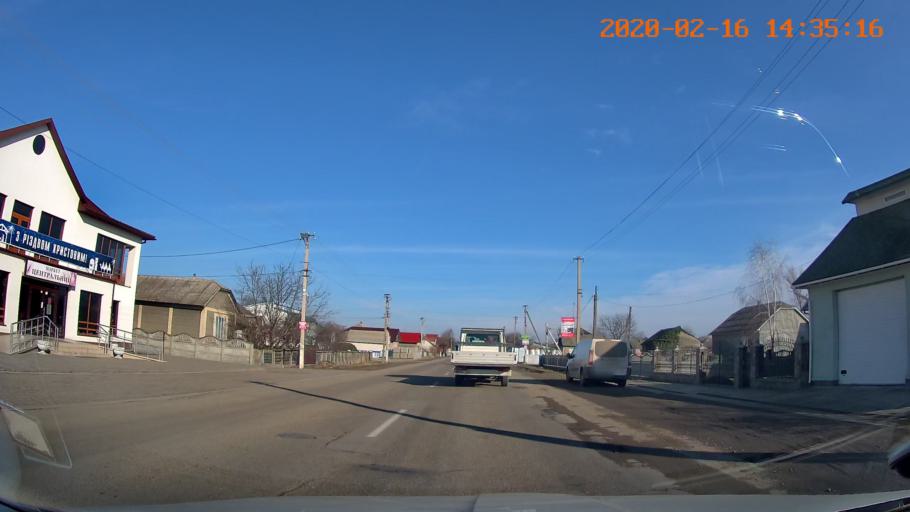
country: RO
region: Botosani
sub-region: Comuna Darabani
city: Bajura
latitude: 48.2228
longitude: 26.4904
